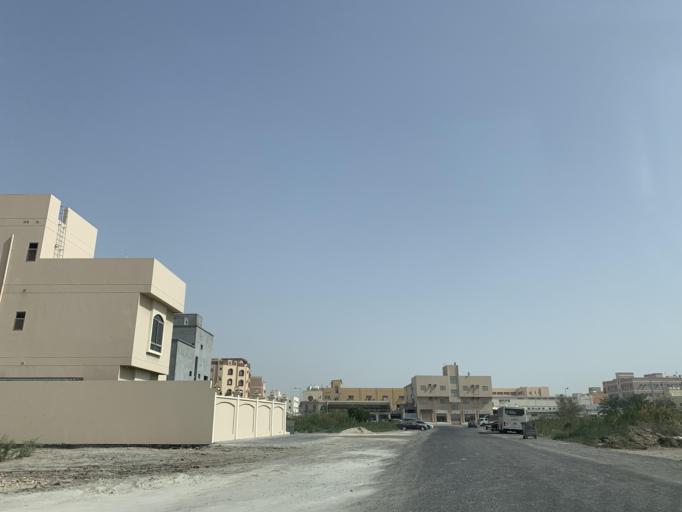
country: BH
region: Northern
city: Madinat `Isa
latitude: 26.1747
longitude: 50.5270
